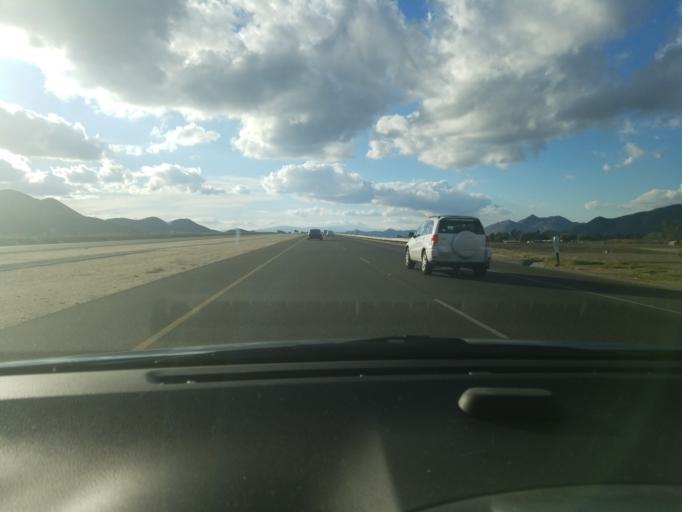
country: US
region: California
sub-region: Riverside County
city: Winchester
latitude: 33.6987
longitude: -117.0434
